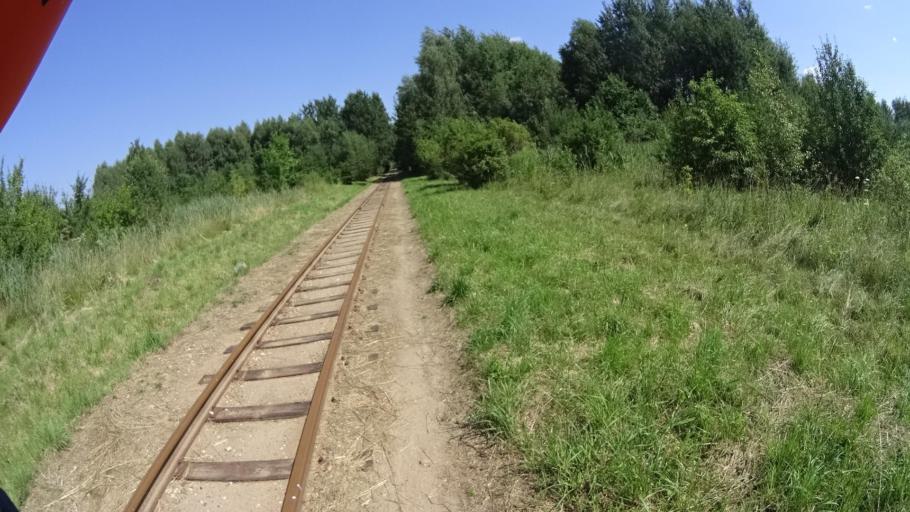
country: PL
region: Masovian Voivodeship
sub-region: Powiat piaseczynski
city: Tarczyn
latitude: 51.9822
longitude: 20.8756
